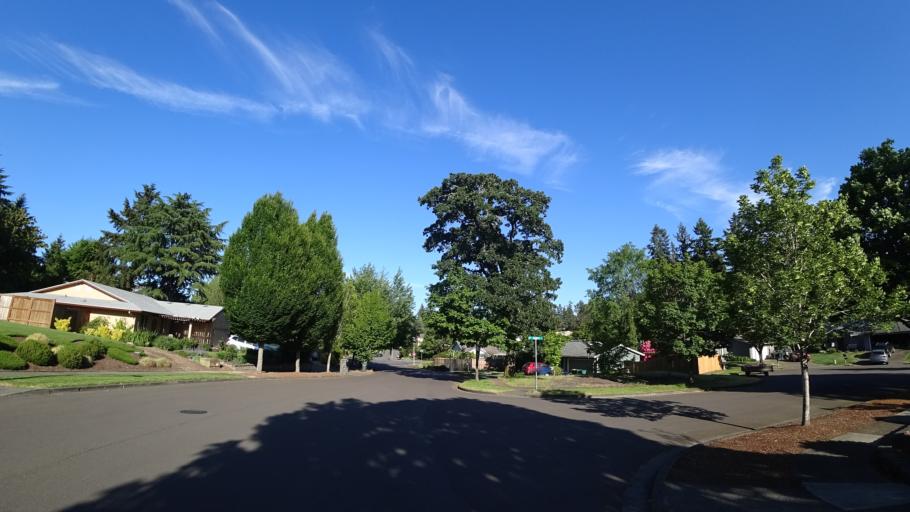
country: US
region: Oregon
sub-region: Washington County
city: Beaverton
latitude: 45.4629
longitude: -122.8092
